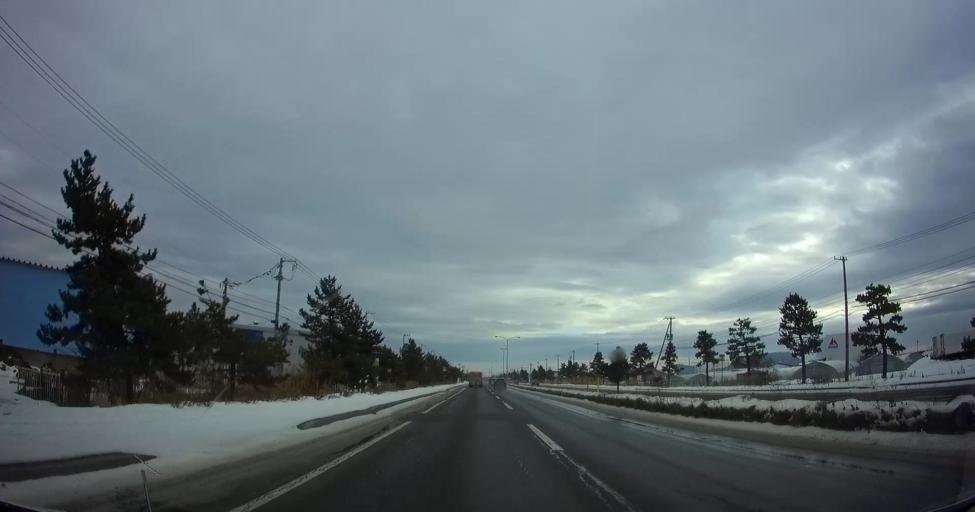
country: JP
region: Hokkaido
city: Nanae
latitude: 41.8452
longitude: 140.6833
